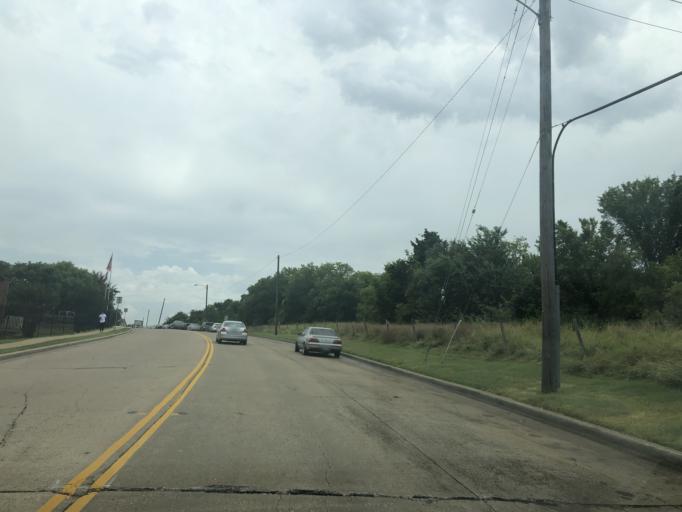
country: US
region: Texas
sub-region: Dallas County
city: Grand Prairie
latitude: 32.7541
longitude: -97.0371
